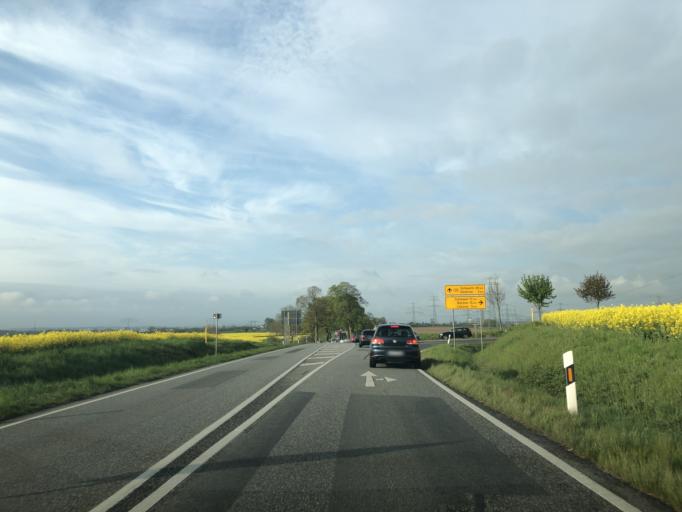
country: DE
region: Mecklenburg-Vorpommern
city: Guestrow
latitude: 53.8260
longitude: 12.2035
